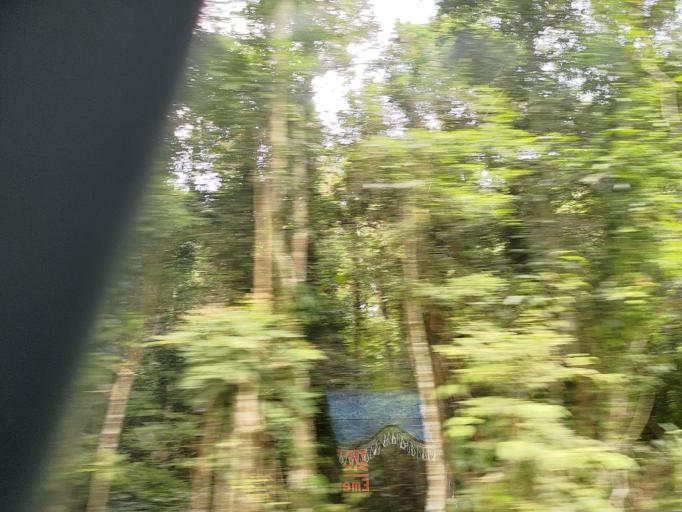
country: TW
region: Taiwan
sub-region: Hsinchu
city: Hsinchu
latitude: 24.6222
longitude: 121.0499
